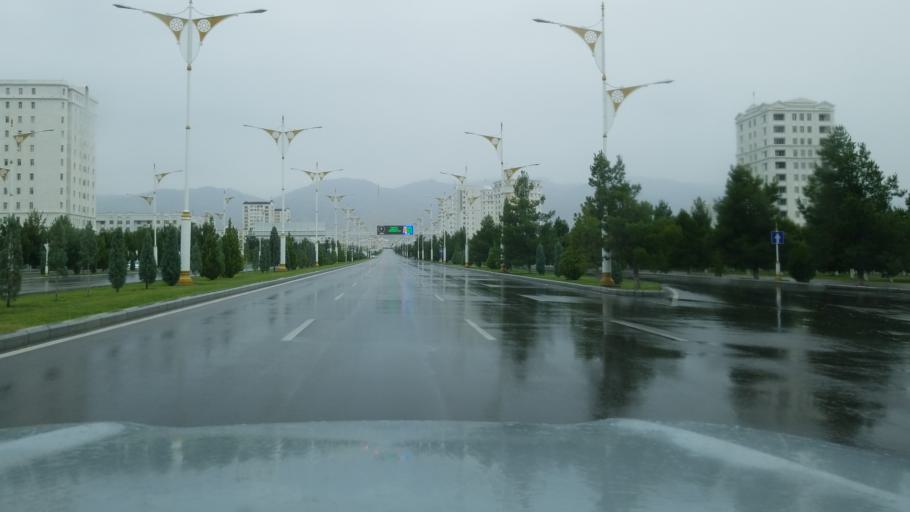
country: TM
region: Ahal
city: Ashgabat
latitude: 37.8975
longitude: 58.3597
